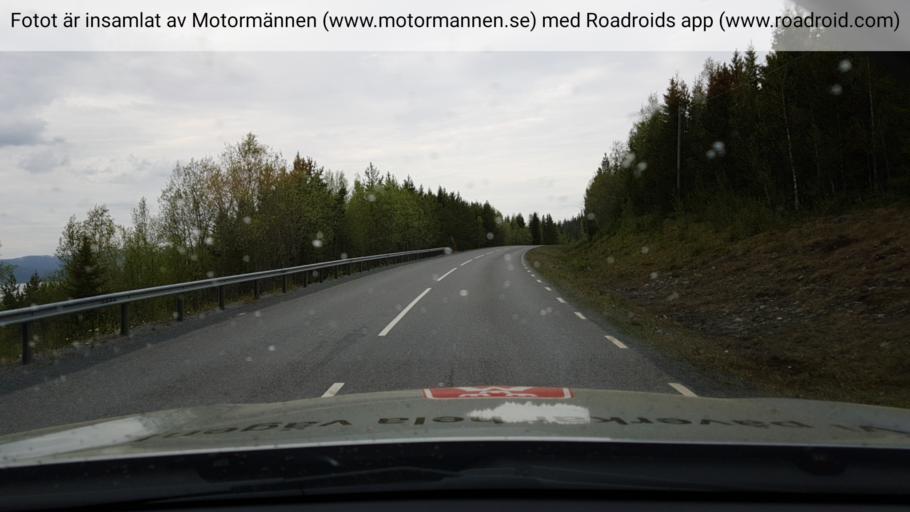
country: SE
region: Jaemtland
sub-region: Are Kommun
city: Are
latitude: 63.5458
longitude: 13.0420
